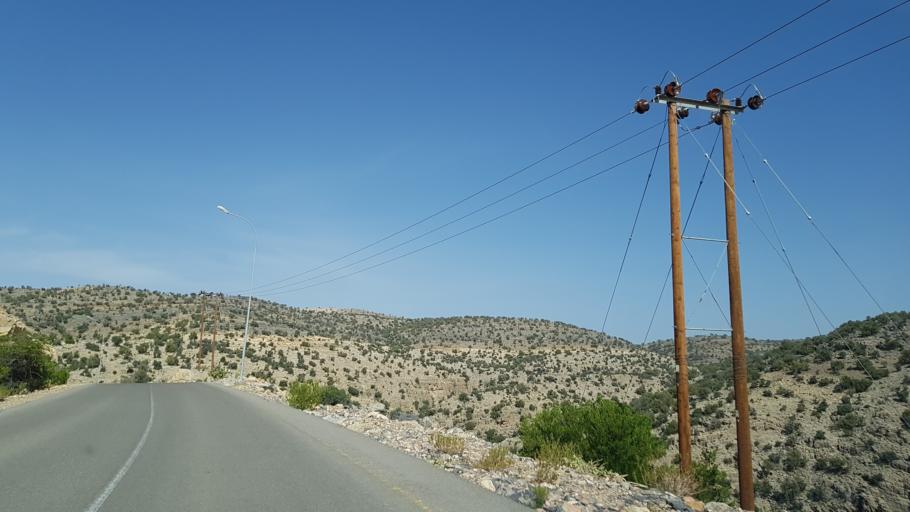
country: OM
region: Al Batinah
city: Bayt al `Awabi
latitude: 23.1390
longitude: 57.5854
